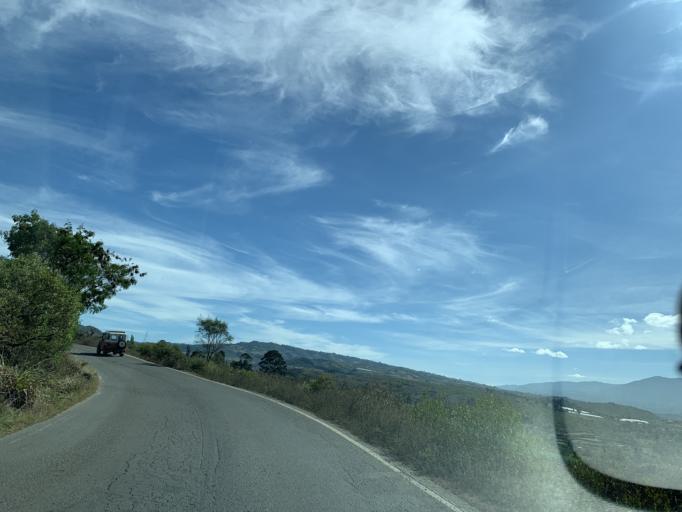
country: CO
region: Boyaca
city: Villa de Leiva
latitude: 5.6693
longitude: -73.5858
